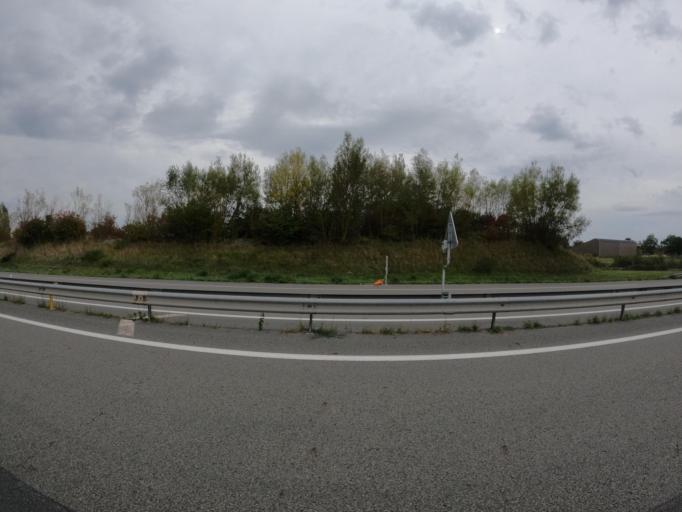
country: FR
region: Limousin
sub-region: Departement de la Creuse
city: Gouzon
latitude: 46.1950
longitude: 2.2202
